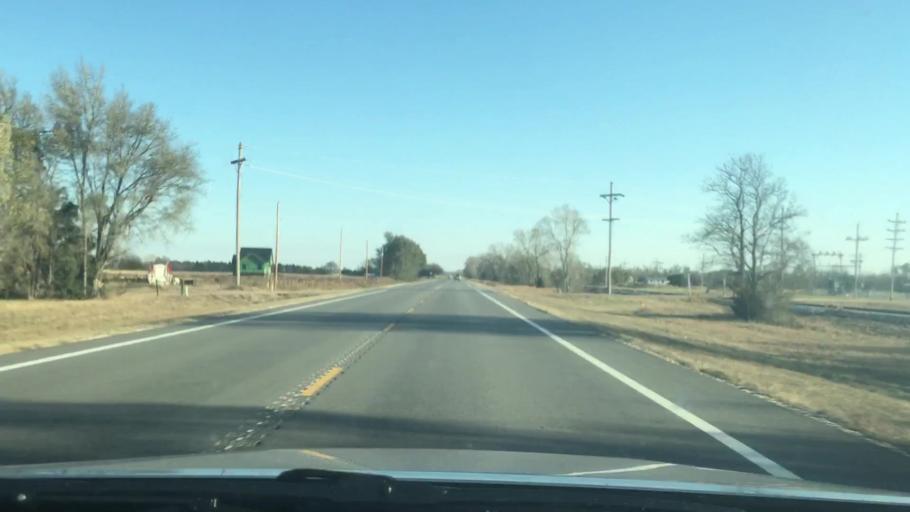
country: US
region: Kansas
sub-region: Reno County
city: Nickerson
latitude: 38.1125
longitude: -98.0327
